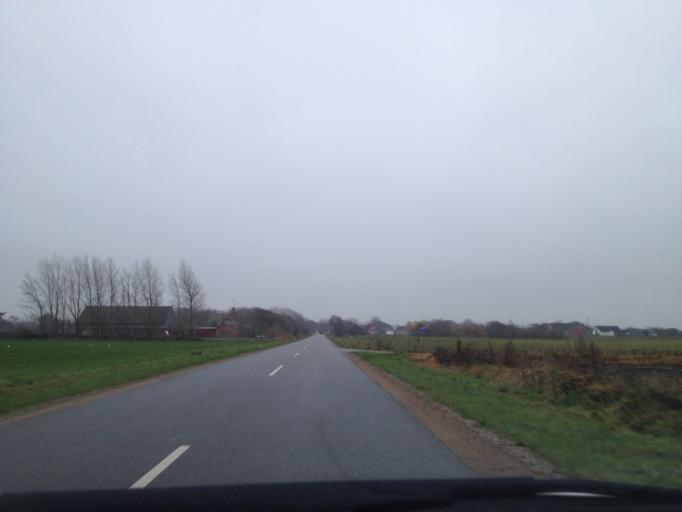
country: DK
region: South Denmark
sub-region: Tonder Kommune
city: Sherrebek
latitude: 55.0915
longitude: 8.7244
